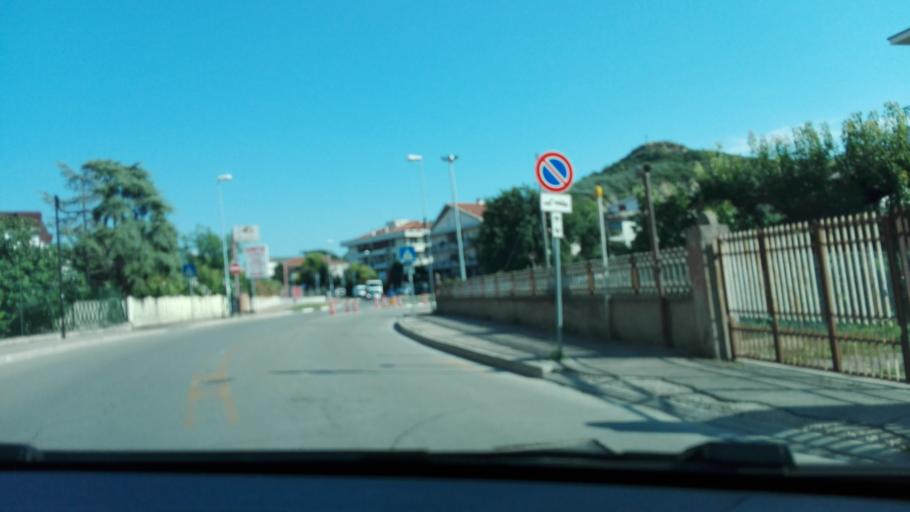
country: IT
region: Abruzzo
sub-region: Provincia di Pescara
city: Montesilvano Marina
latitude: 42.5111
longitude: 14.1528
